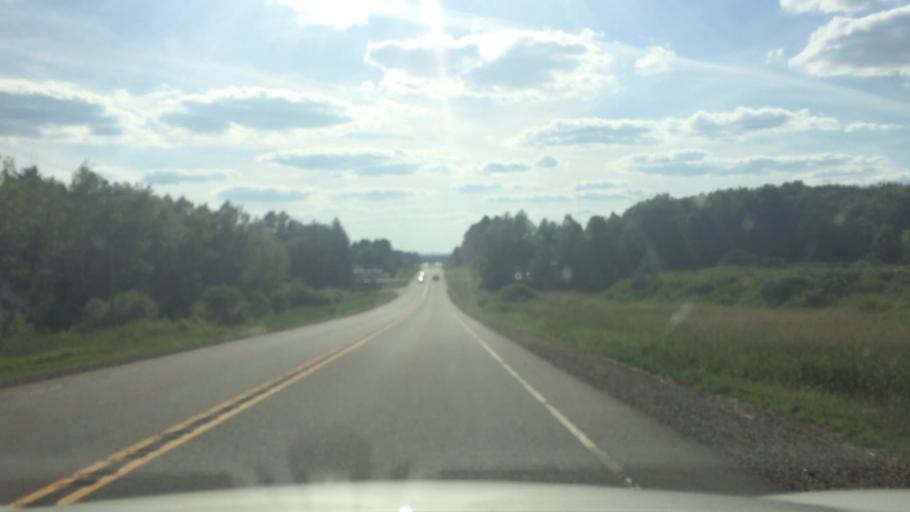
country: US
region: Wisconsin
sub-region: Lincoln County
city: Merrill
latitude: 45.1779
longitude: -89.6284
